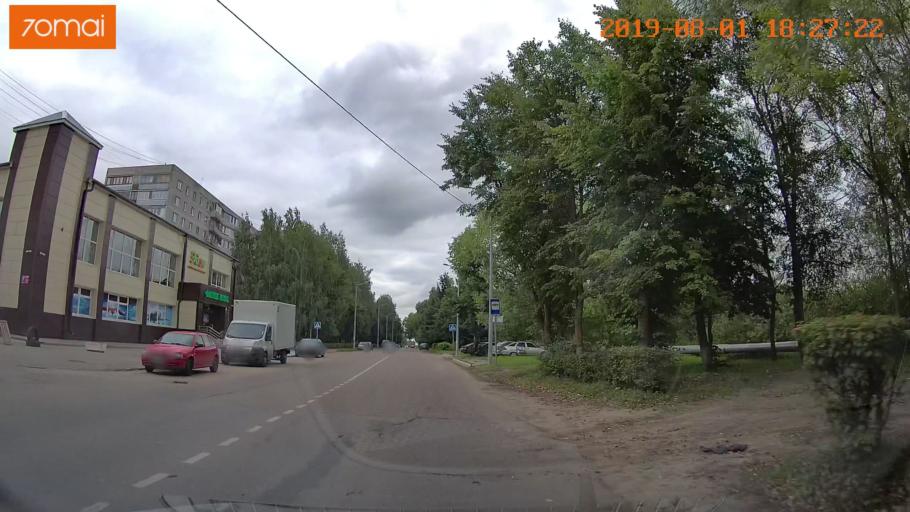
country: RU
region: Moskovskaya
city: Voskresensk
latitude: 55.3127
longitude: 38.6432
